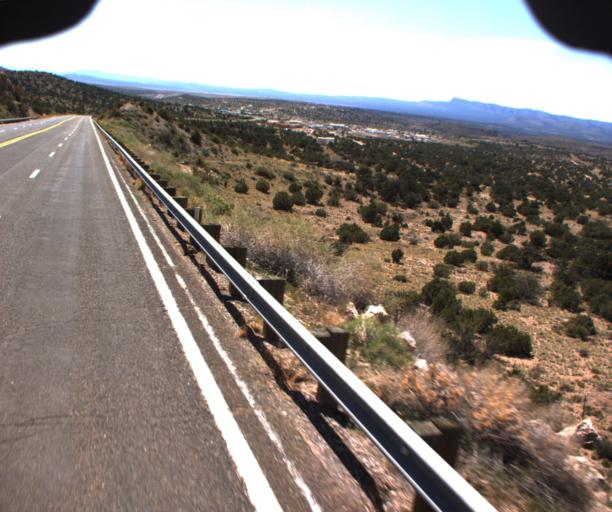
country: US
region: Arizona
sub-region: Mohave County
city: Peach Springs
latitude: 35.5459
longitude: -113.3996
